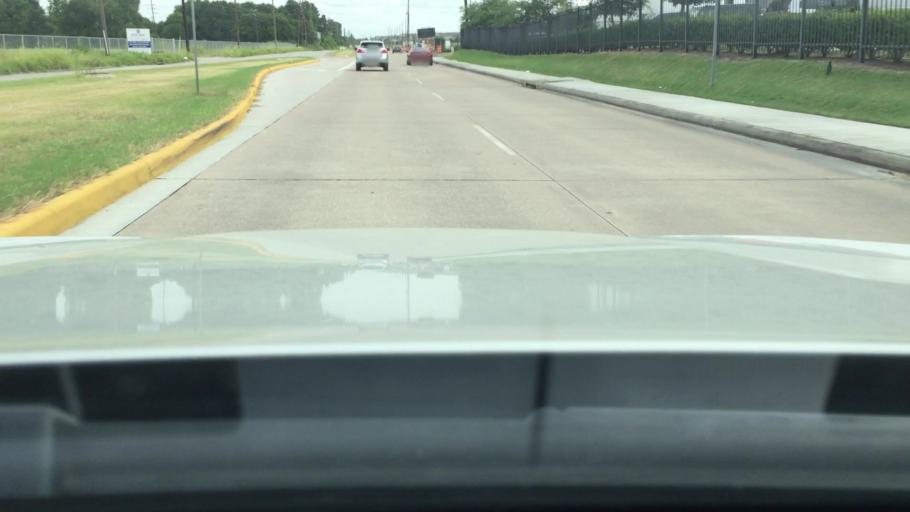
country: US
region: Texas
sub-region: Harris County
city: Jersey Village
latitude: 29.9407
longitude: -95.5467
